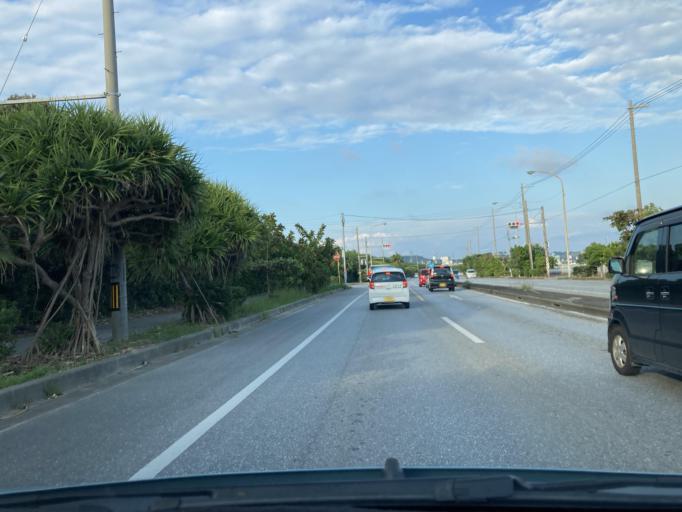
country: JP
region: Okinawa
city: Okinawa
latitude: 26.3281
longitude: 127.8354
